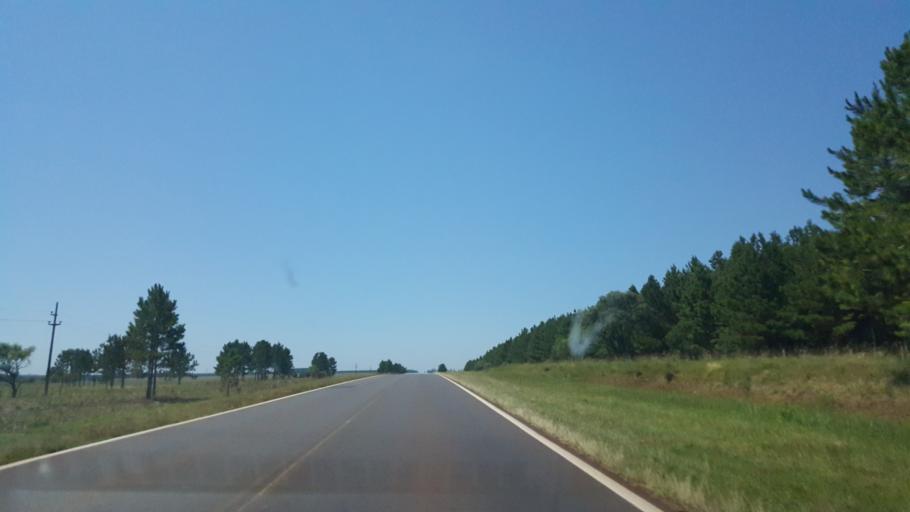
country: AR
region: Corrientes
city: Santo Tome
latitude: -28.3895
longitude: -56.1076
